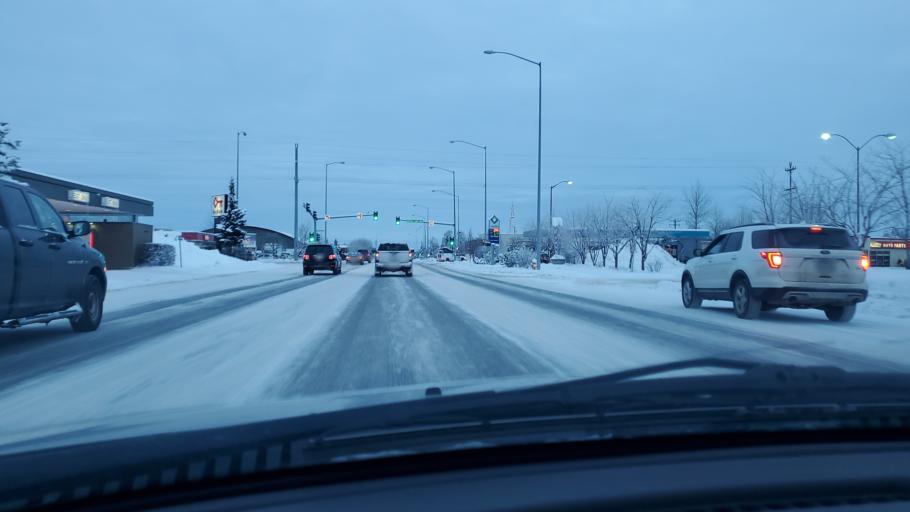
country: US
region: Alaska
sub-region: Anchorage Municipality
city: Anchorage
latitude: 61.1945
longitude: -149.8831
